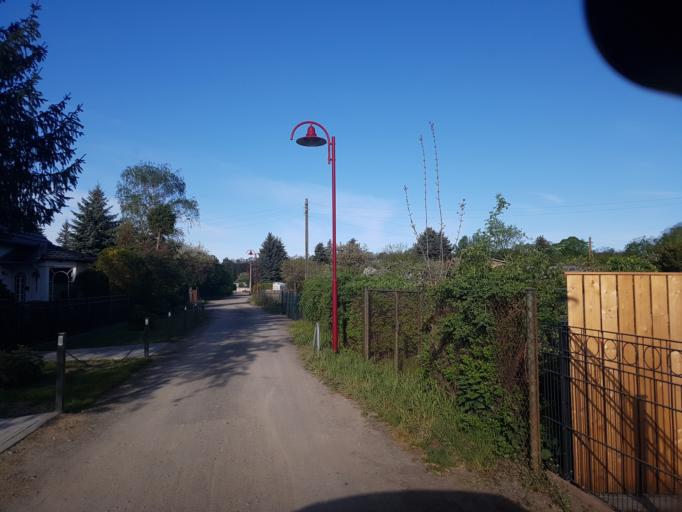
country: DE
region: Brandenburg
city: Finsterwalde
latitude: 51.6262
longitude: 13.6967
